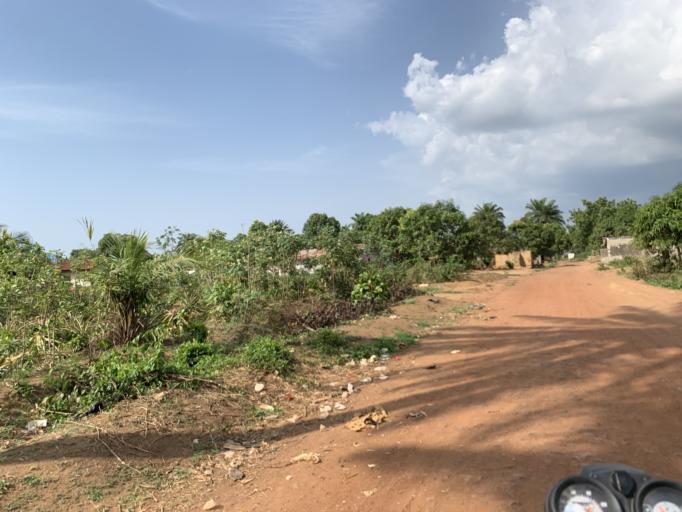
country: SL
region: Western Area
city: Waterloo
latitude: 8.3435
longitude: -13.0480
